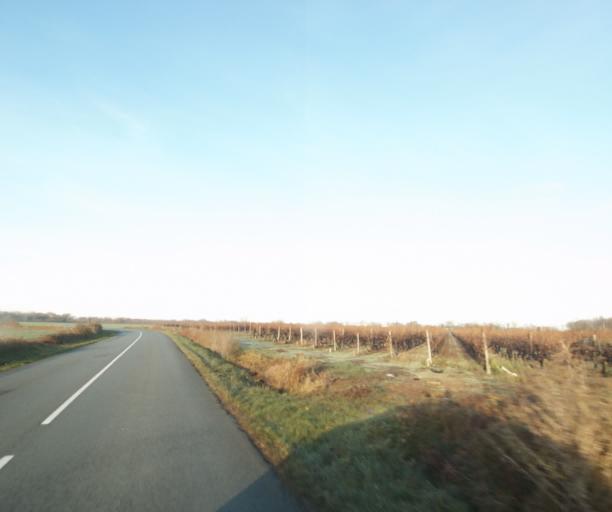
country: FR
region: Poitou-Charentes
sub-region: Departement de la Charente-Maritime
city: Fontcouverte
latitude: 45.7737
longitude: -0.5674
